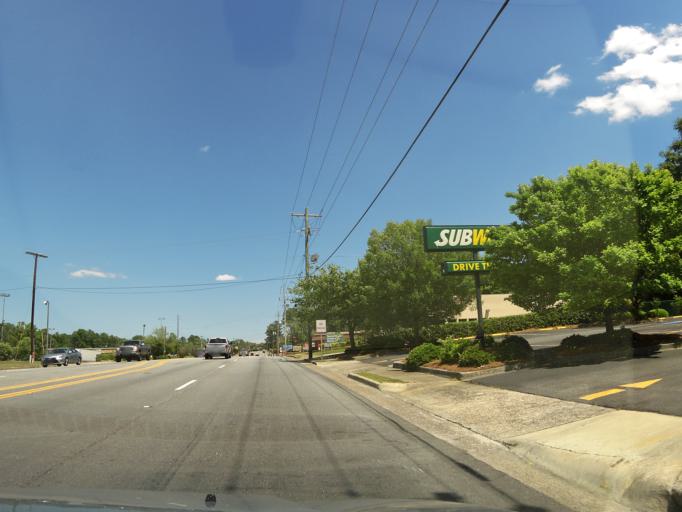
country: US
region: South Carolina
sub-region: Aiken County
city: Aiken
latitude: 33.5649
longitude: -81.7440
